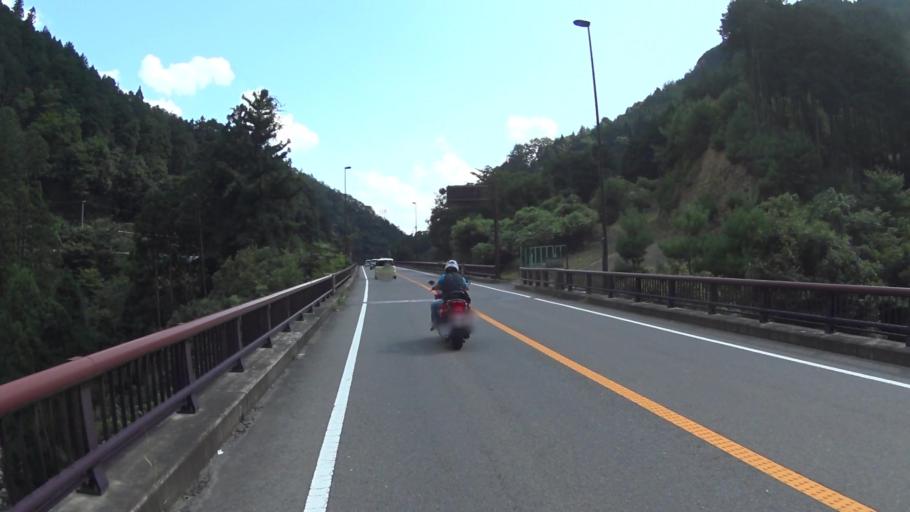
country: JP
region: Kyoto
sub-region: Kyoto-shi
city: Kamigyo-ku
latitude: 35.0749
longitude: 135.6857
